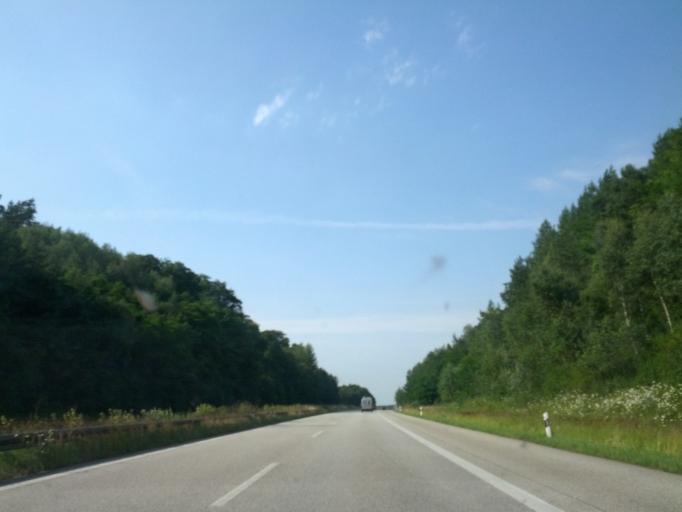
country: DE
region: Mecklenburg-Vorpommern
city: Lalendorf
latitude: 53.7471
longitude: 12.3320
